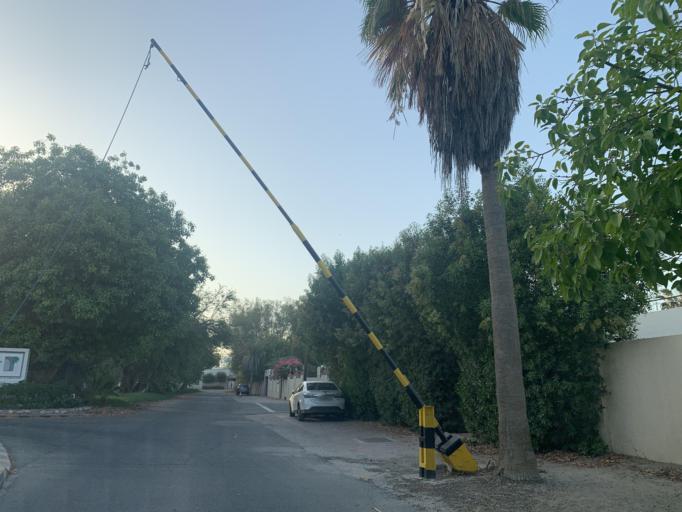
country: BH
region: Manama
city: Jidd Hafs
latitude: 26.2208
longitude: 50.5307
